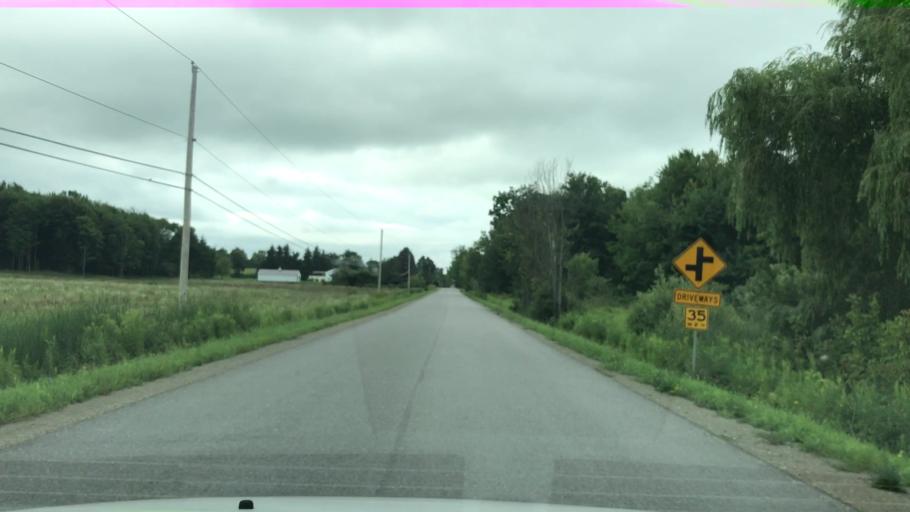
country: US
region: New York
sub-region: Wyoming County
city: Attica
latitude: 42.8264
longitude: -78.3362
